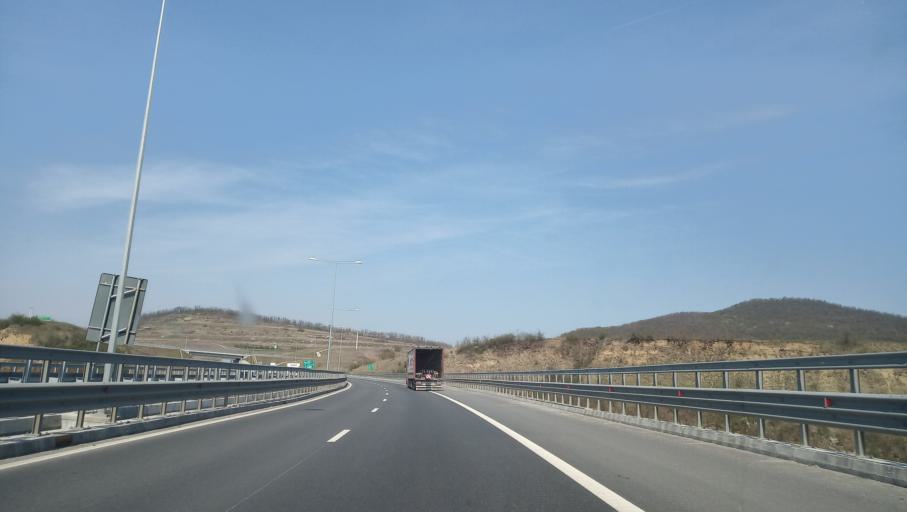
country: RO
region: Alba
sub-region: Municipiul Aiud
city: Aiud
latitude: 46.3391
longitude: 23.7337
